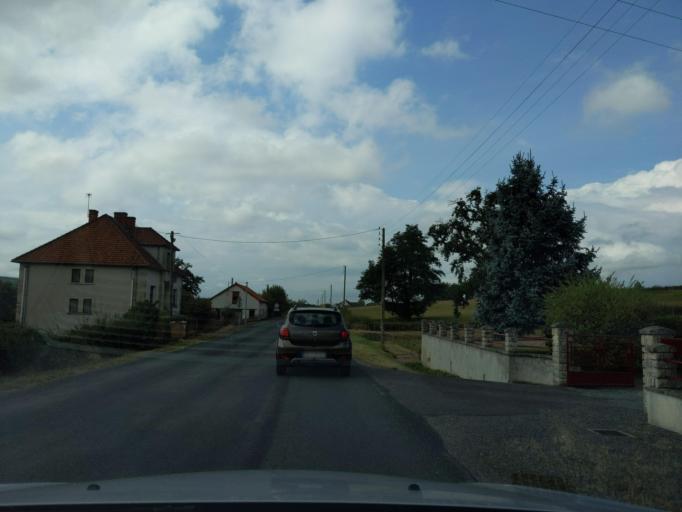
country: FR
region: Bourgogne
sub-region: Departement de Saone-et-Loire
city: Bourbon-Lancy
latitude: 46.6802
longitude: 3.8155
